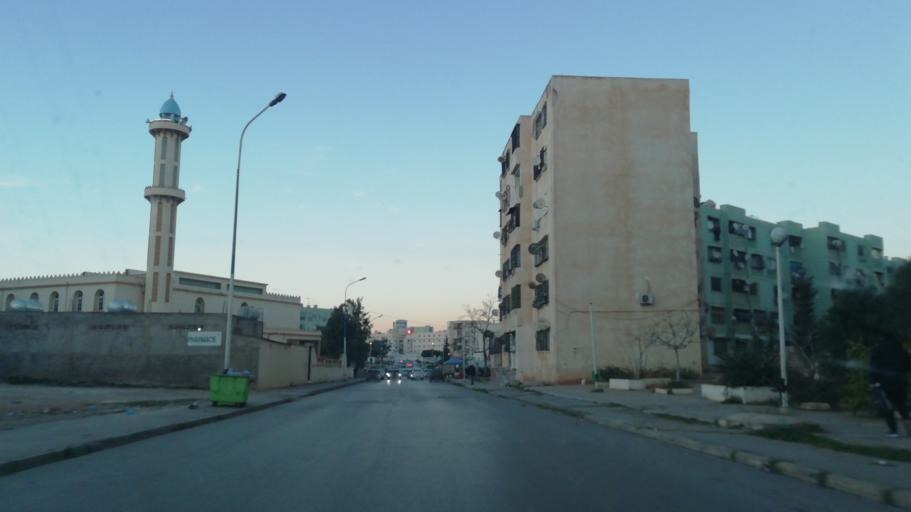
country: DZ
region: Oran
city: Oran
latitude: 35.6990
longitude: -0.5955
